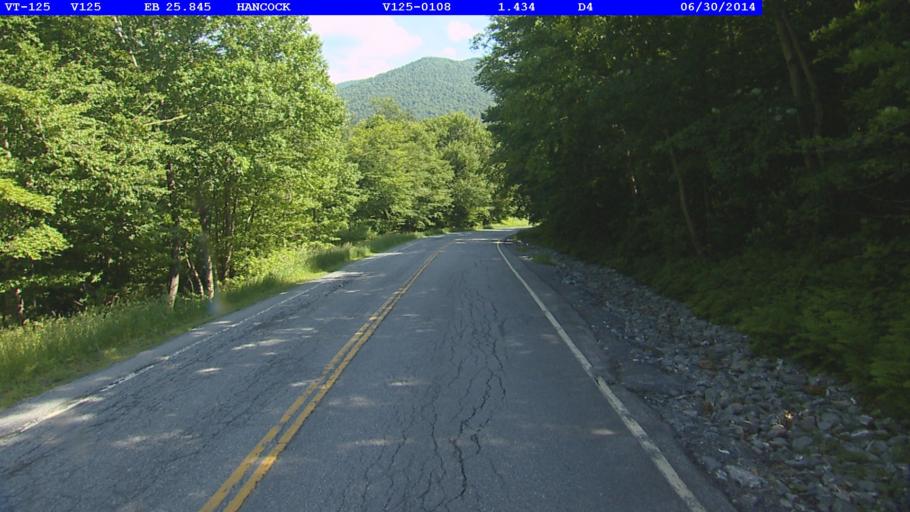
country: US
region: Vermont
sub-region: Rutland County
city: Brandon
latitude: 43.9325
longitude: -72.9468
